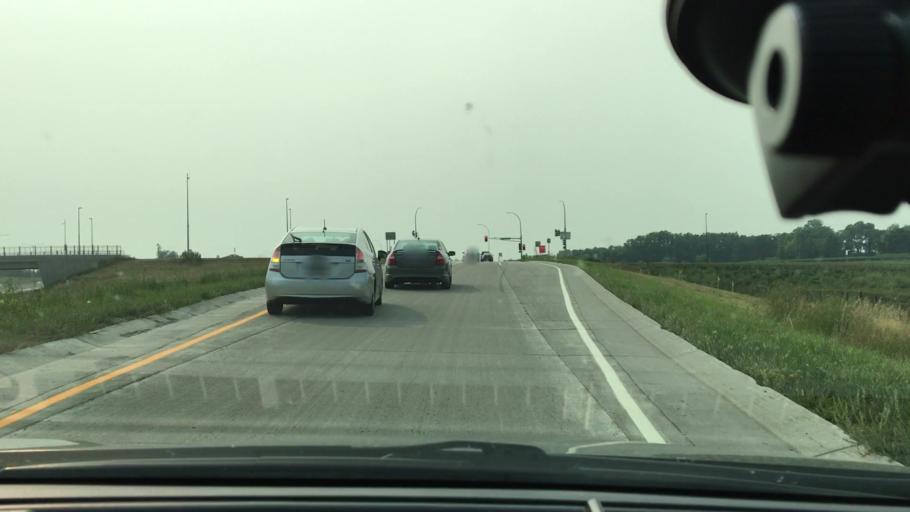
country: US
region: Minnesota
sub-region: Hennepin County
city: Maple Grove
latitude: 45.1380
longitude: -93.4697
